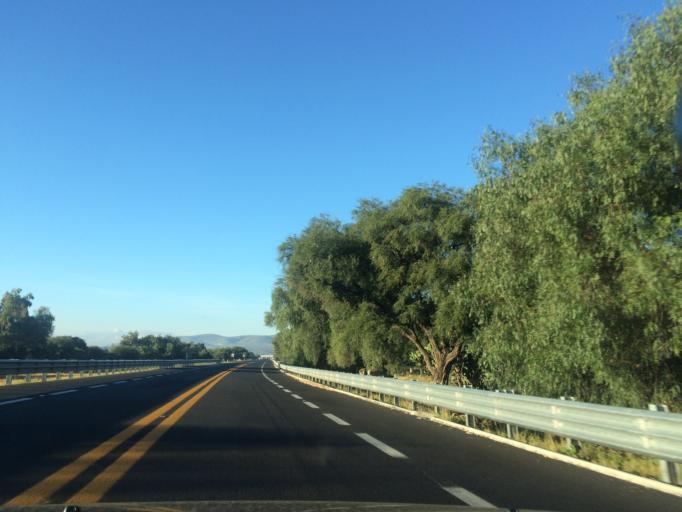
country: MX
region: Puebla
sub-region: Santiago Miahuatlan
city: San Jose Monte Chiquito
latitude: 18.5207
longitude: -97.4544
